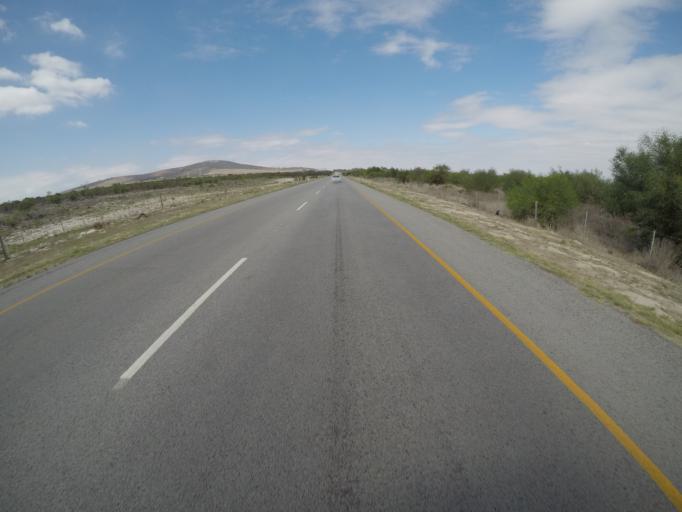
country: ZA
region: Western Cape
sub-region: City of Cape Town
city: Sunset Beach
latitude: -33.7248
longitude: 18.5276
